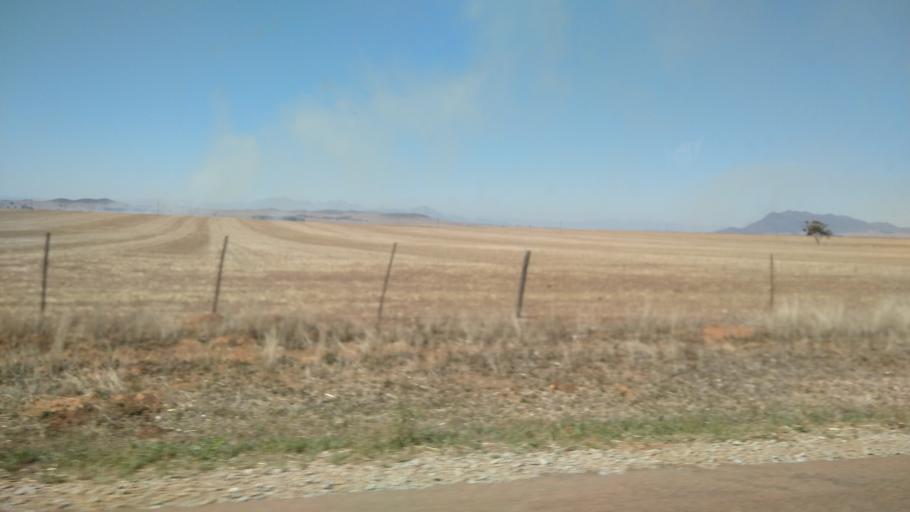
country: ZA
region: Western Cape
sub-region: West Coast District Municipality
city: Moorreesburg
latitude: -33.3055
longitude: 18.6169
